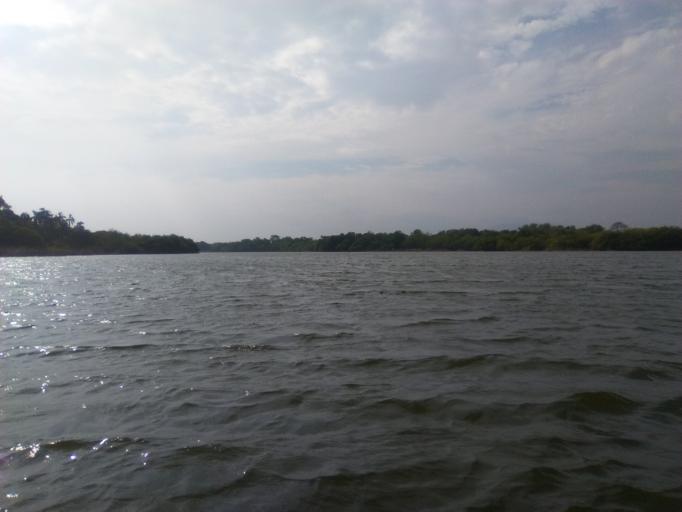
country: MX
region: Guerrero
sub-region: Coyuca de Benitez
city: El Embarcadero
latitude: 16.9570
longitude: -100.0373
